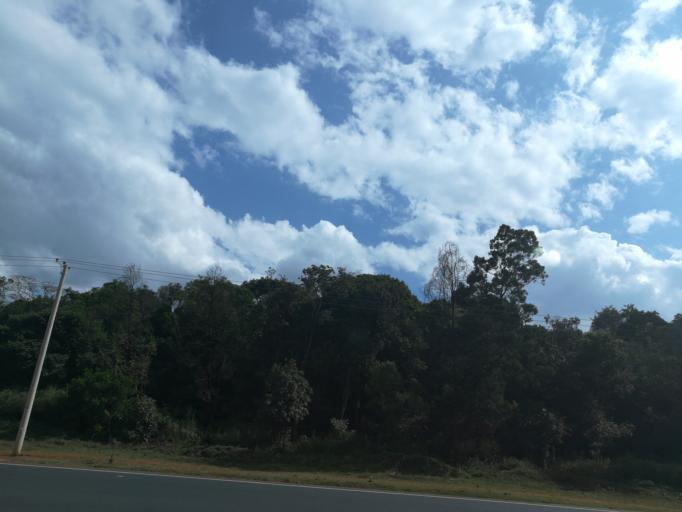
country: KE
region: Nairobi Area
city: Nairobi
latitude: -1.3222
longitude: 36.7370
